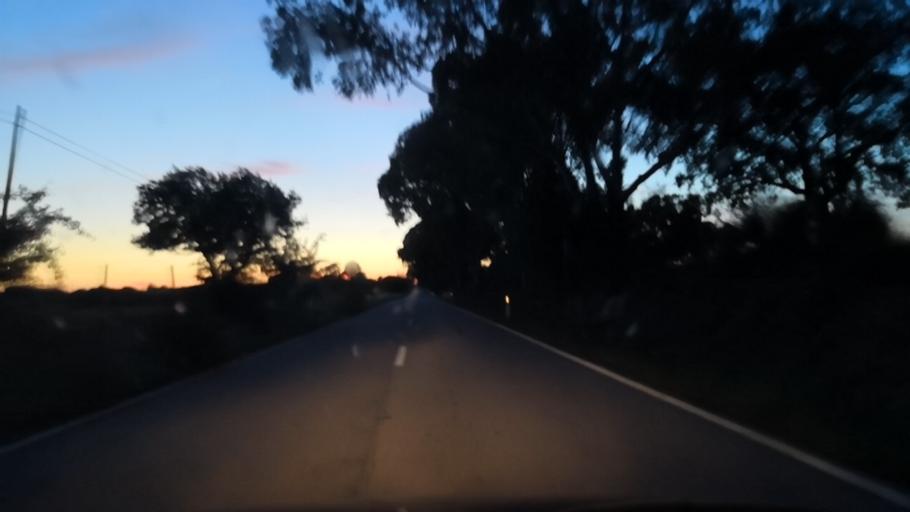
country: ES
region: Extremadura
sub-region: Provincia de Caceres
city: Piedras Albas
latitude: 39.8633
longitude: -7.0102
